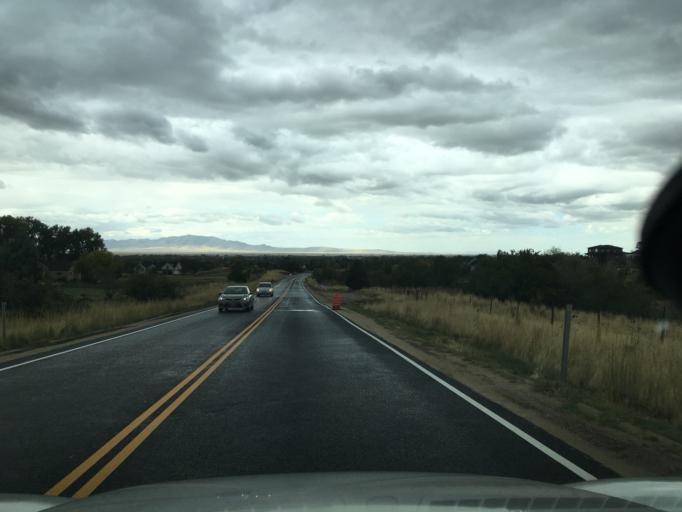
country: US
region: Utah
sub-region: Davis County
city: Kaysville
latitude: 41.0633
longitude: -111.9296
